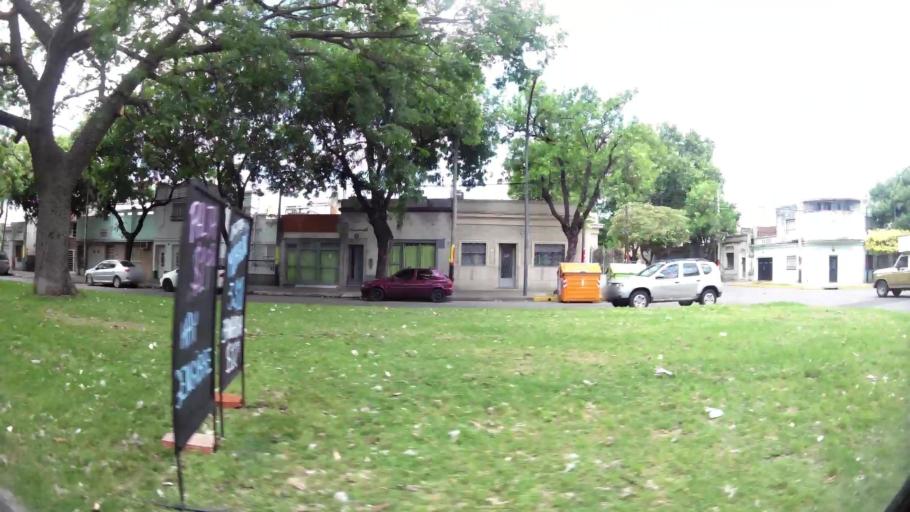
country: AR
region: Santa Fe
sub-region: Departamento de Rosario
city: Rosario
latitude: -32.9798
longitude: -60.6424
